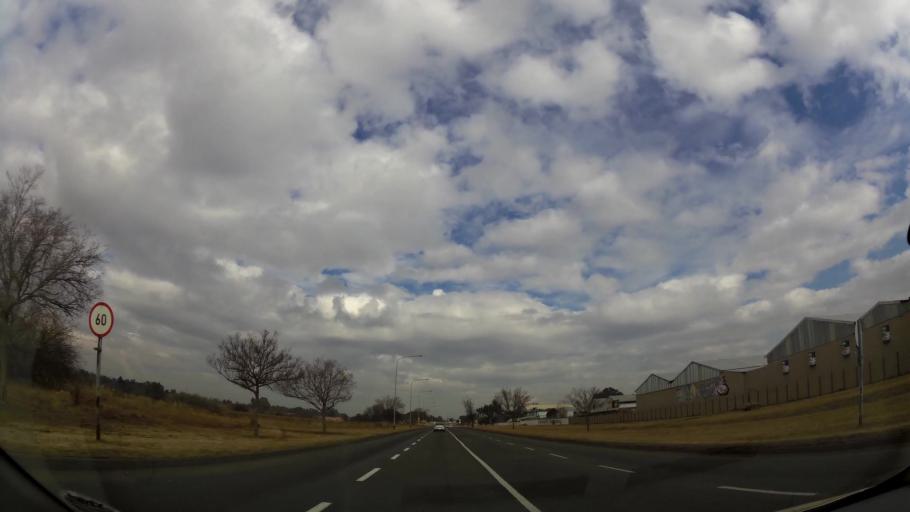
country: ZA
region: Gauteng
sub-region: Sedibeng District Municipality
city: Meyerton
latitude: -26.5788
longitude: 28.0169
